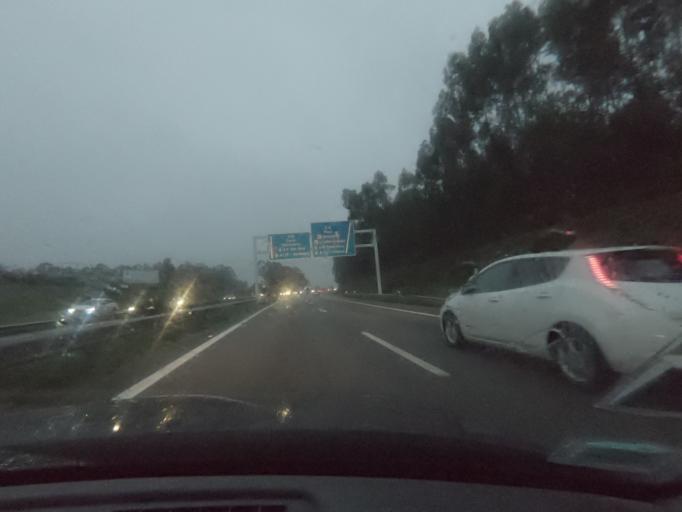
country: PT
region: Porto
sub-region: Matosinhos
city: Santa Cruz do Bispo
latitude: 41.2441
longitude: -8.6945
